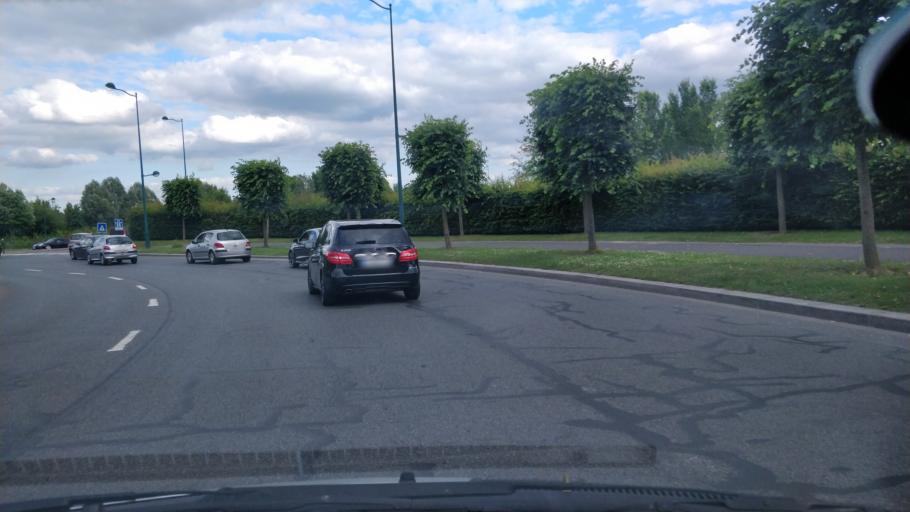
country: FR
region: Ile-de-France
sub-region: Departement de Seine-et-Marne
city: Serris
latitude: 48.8520
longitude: 2.7772
